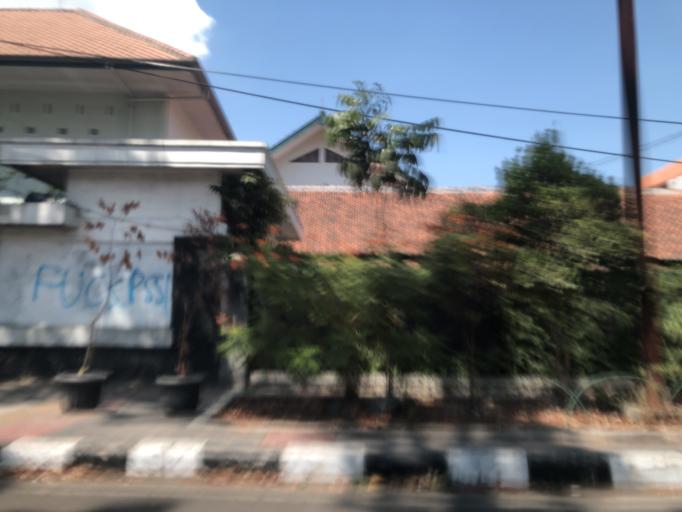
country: ID
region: West Java
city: Bandung
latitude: -6.9132
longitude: 107.6329
